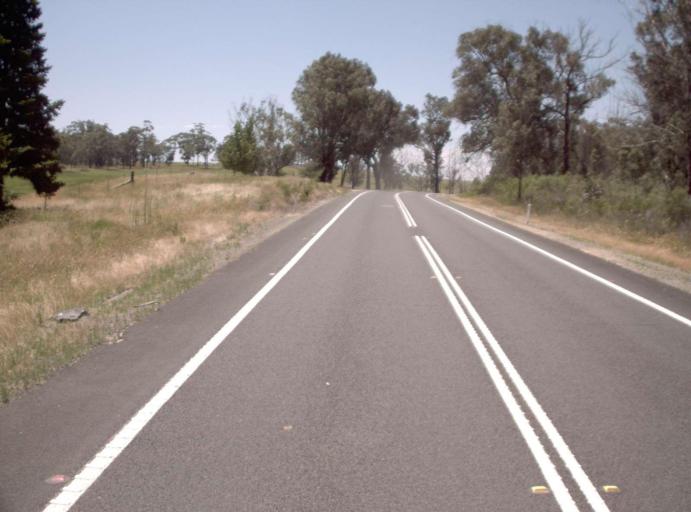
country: AU
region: Victoria
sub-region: East Gippsland
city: Lakes Entrance
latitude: -37.7555
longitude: 148.2771
